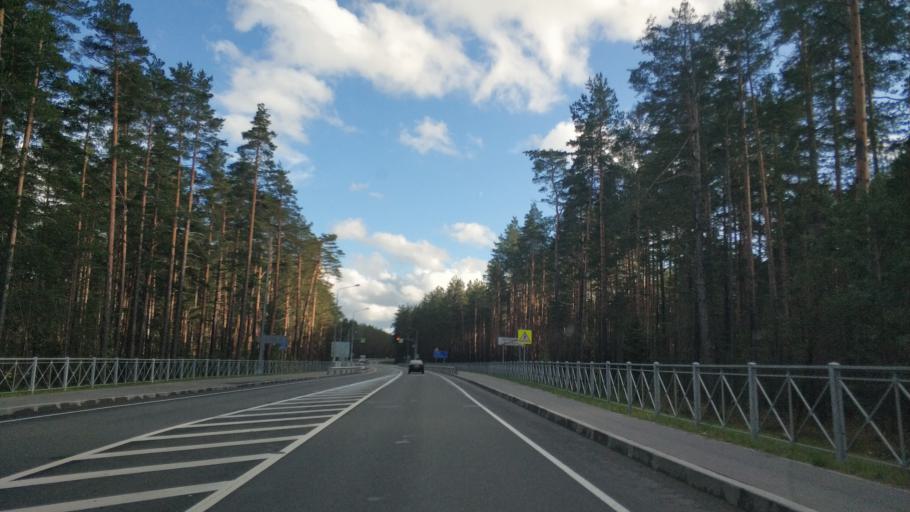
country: RU
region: Leningrad
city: Priozersk
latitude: 60.9959
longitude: 30.1822
